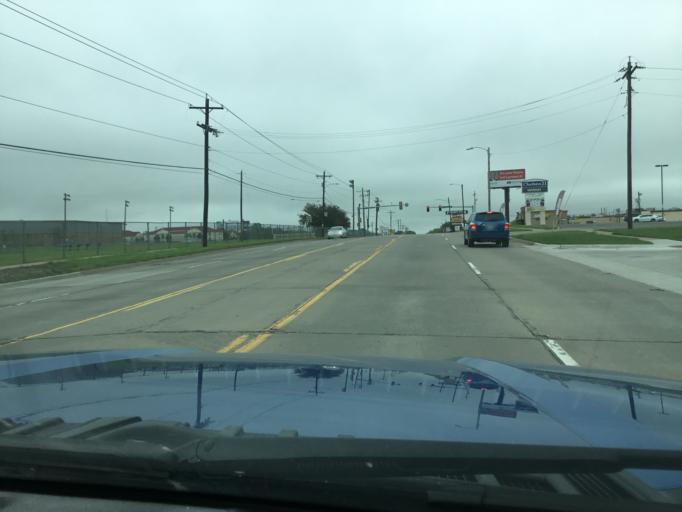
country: US
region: Kansas
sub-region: Shawnee County
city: Topeka
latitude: 39.0292
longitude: -95.7495
